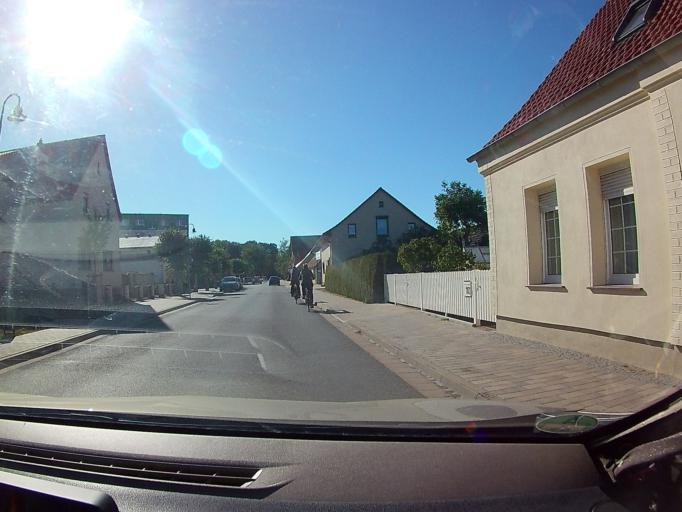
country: DE
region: Mecklenburg-Vorpommern
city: Wesenberg
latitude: 53.2827
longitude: 12.9653
